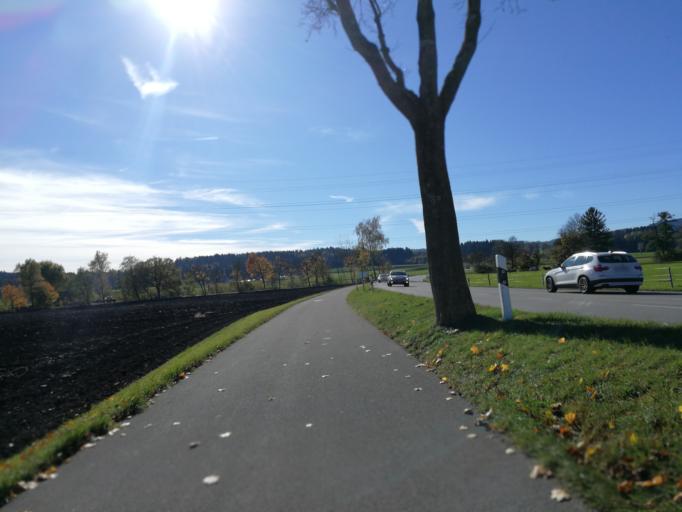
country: CH
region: Zurich
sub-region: Bezirk Hinwil
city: Gossau
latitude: 47.3018
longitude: 8.7495
